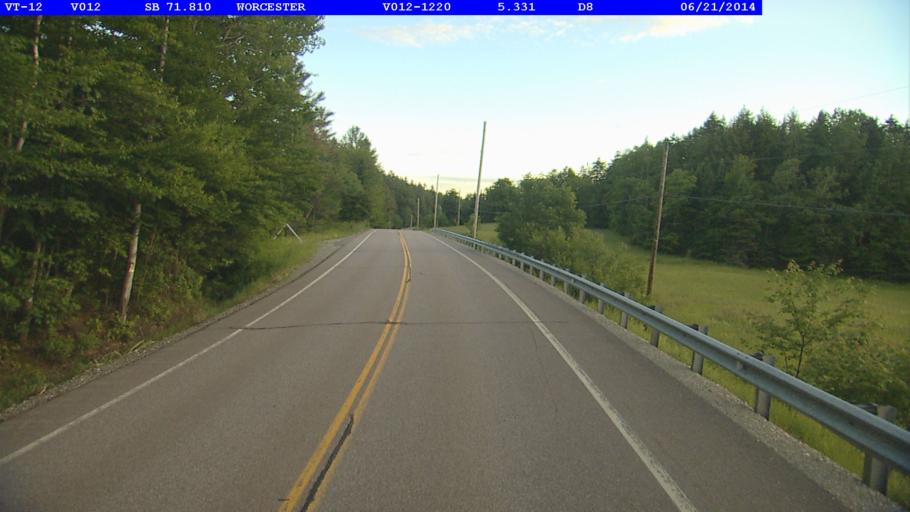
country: US
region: Vermont
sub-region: Lamoille County
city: Morrisville
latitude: 44.4212
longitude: -72.5427
